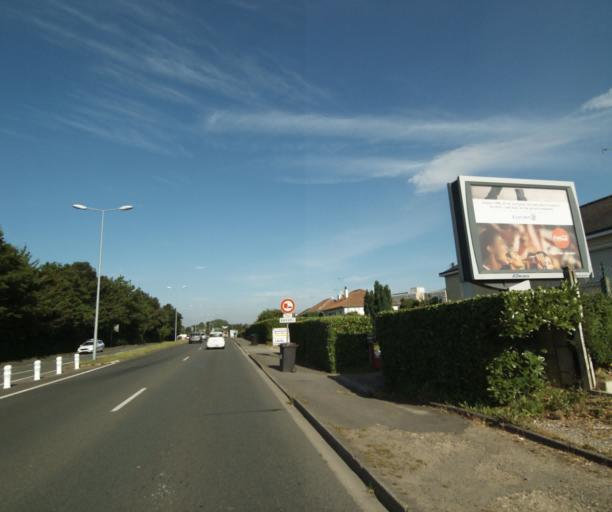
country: FR
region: Pays de la Loire
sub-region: Departement de la Mayenne
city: Laval
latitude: 48.0600
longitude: -0.7767
